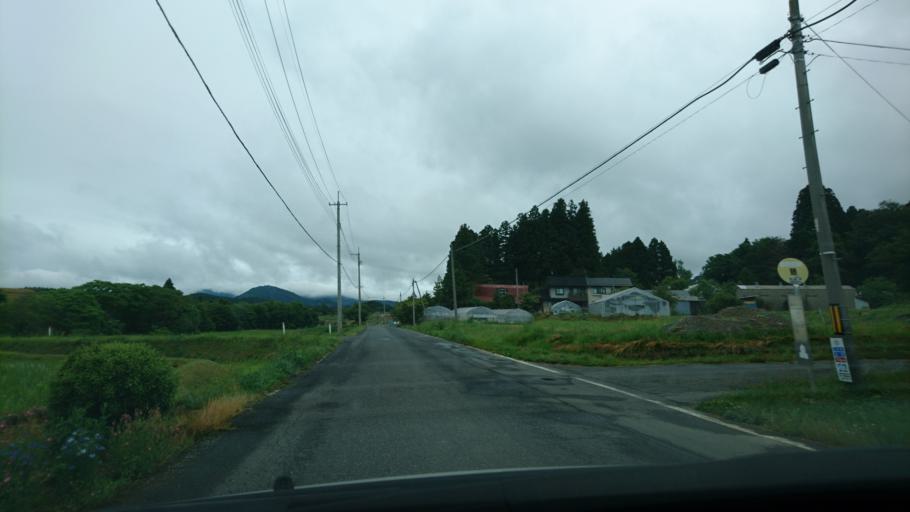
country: JP
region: Iwate
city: Ichinoseki
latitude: 38.9188
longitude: 141.2087
